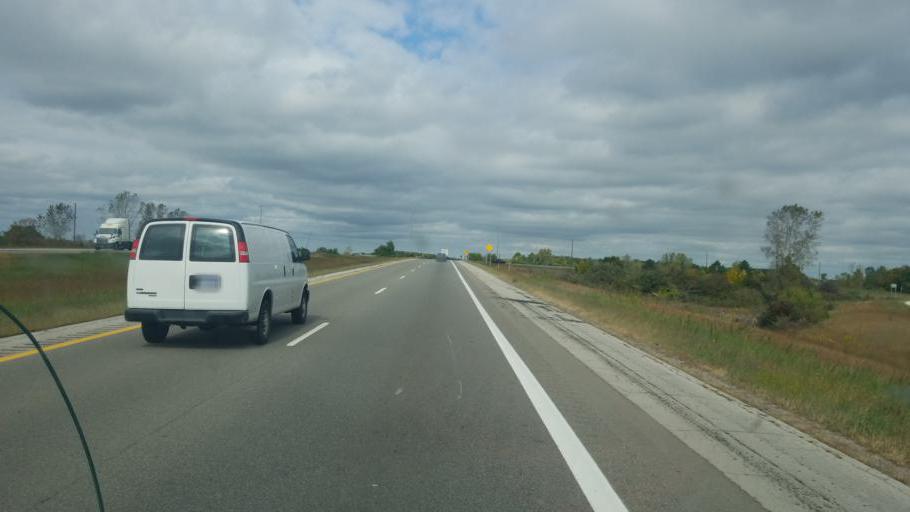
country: US
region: Michigan
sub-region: Monroe County
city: Carleton
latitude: 42.0158
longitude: -83.3446
